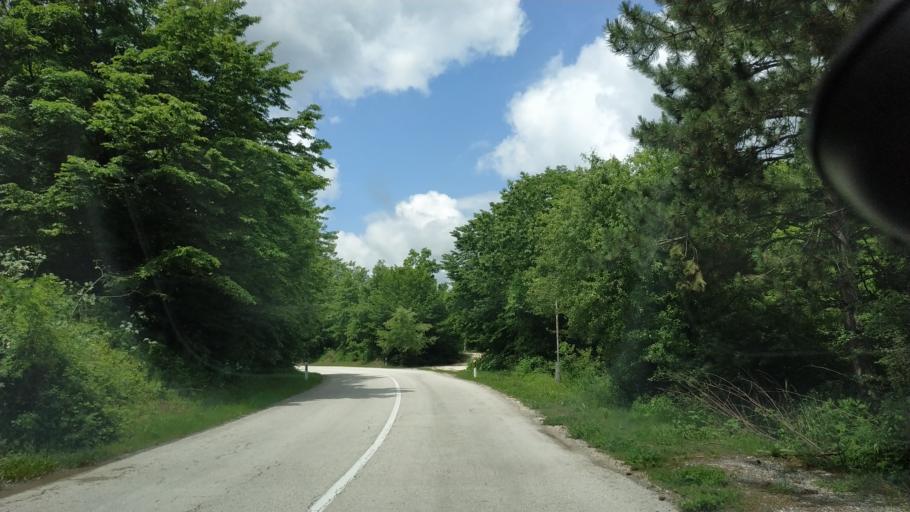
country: RS
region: Central Serbia
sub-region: Borski Okrug
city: Bor
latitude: 44.0868
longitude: 22.0008
